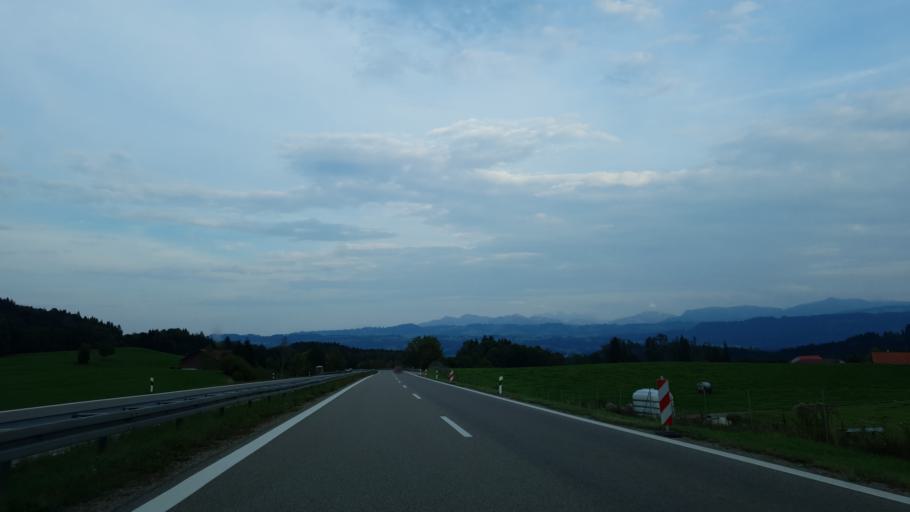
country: DE
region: Bavaria
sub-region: Swabia
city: Buchenberg
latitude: 47.6699
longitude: 10.2435
